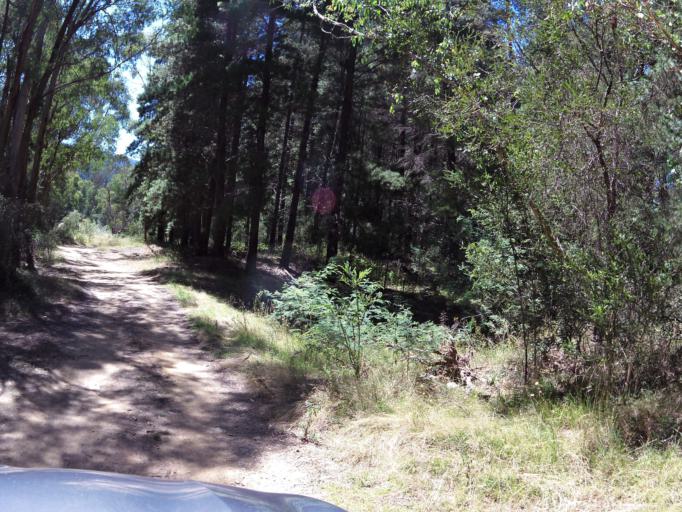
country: AU
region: Victoria
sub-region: Alpine
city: Mount Beauty
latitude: -36.7257
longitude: 146.9867
